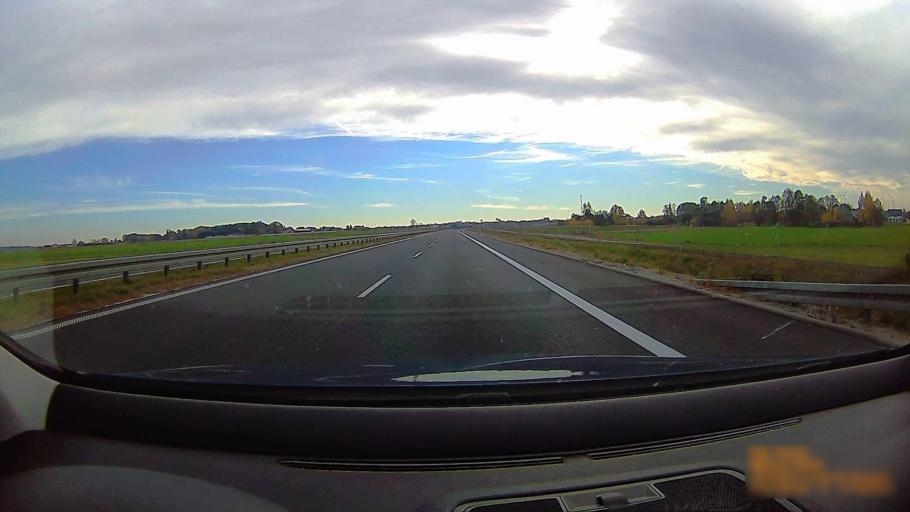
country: PL
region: Greater Poland Voivodeship
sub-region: Powiat ostrowski
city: Ostrow Wielkopolski
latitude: 51.6498
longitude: 17.8712
